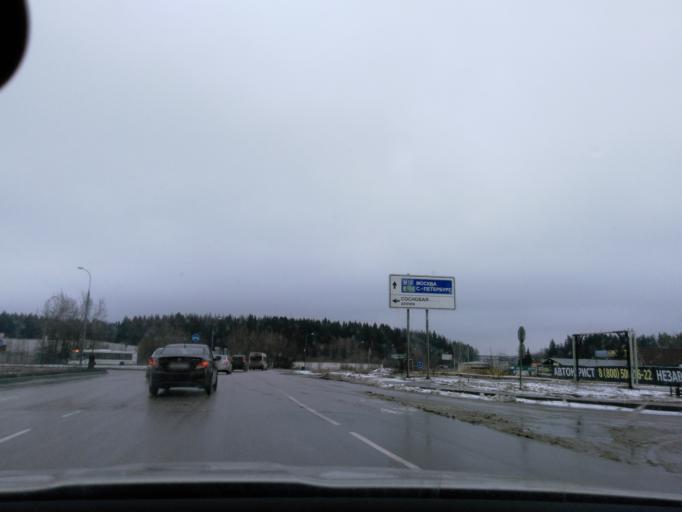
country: RU
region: Moskovskaya
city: Rzhavki
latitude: 55.9801
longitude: 37.2649
